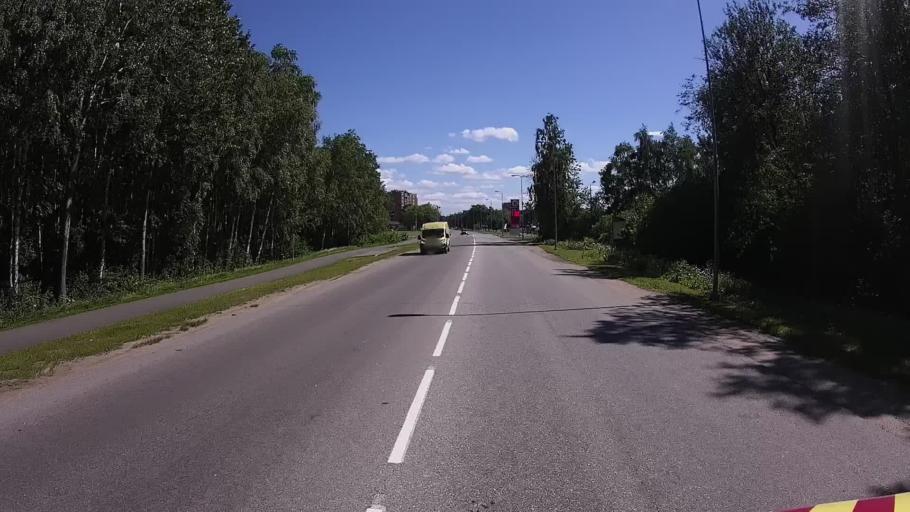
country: EE
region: Ida-Virumaa
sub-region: Kohtla-Jaerve linn
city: Kohtla-Jarve
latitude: 59.4112
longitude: 27.2778
